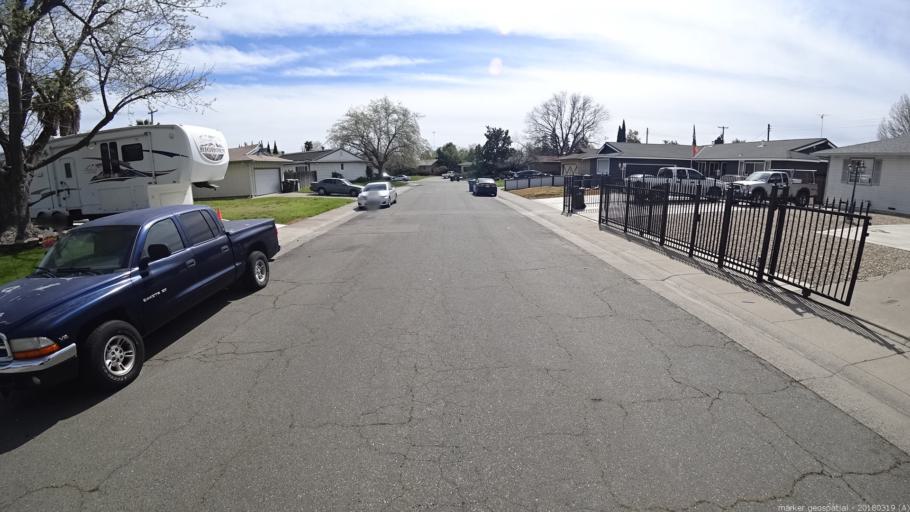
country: US
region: California
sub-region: Sacramento County
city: Parkway
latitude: 38.5053
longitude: -121.4474
